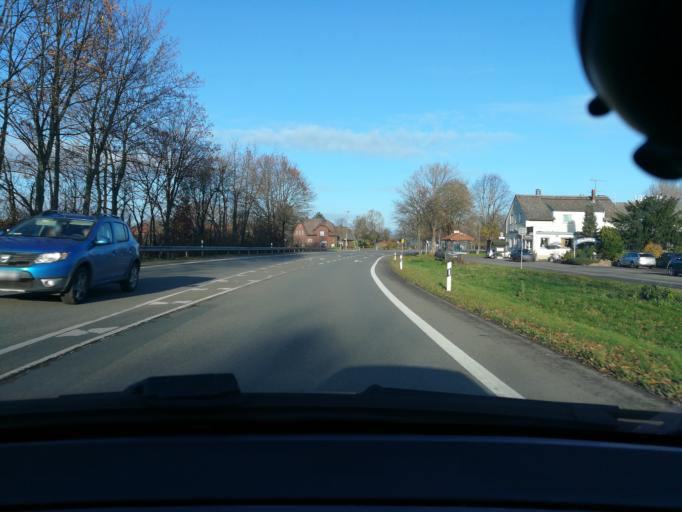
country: DE
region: North Rhine-Westphalia
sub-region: Regierungsbezirk Detmold
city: Petershagen
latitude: 52.3318
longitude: 8.9526
